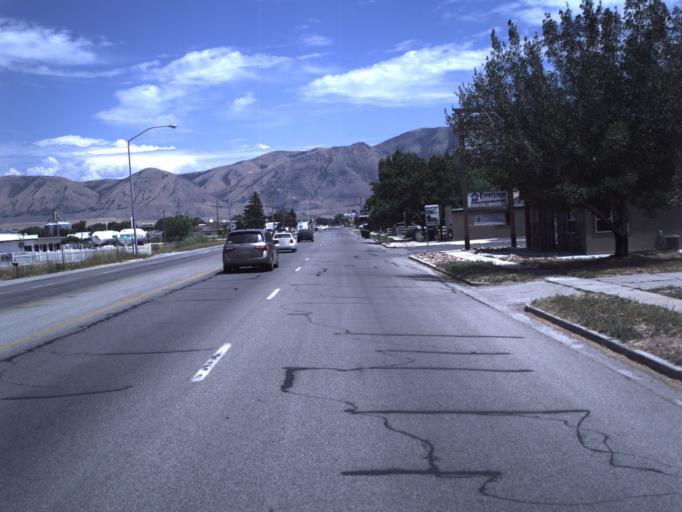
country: US
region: Utah
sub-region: Box Elder County
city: Tremonton
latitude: 41.7113
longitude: -112.1784
